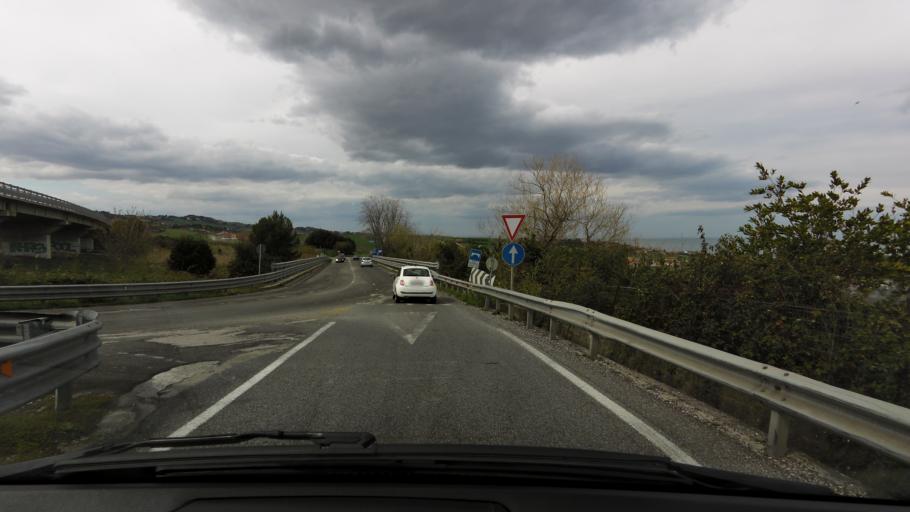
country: IT
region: The Marches
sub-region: Provincia di Ancona
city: Posatora
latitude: 43.5966
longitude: 13.4516
